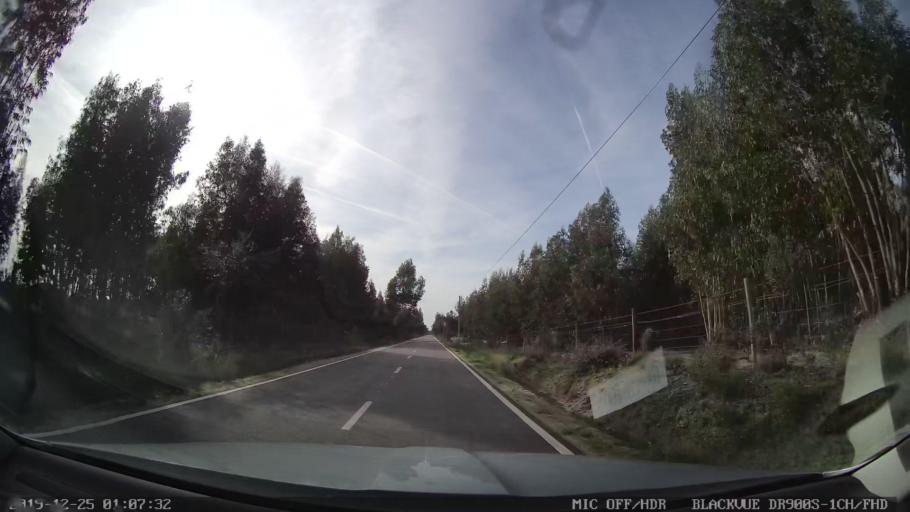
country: PT
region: Portalegre
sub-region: Nisa
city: Nisa
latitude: 39.4612
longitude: -7.7031
